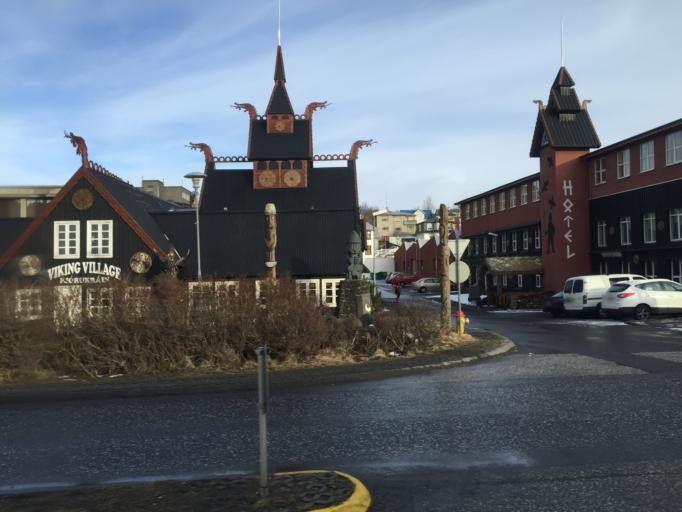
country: IS
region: Capital Region
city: Hafnarfjoerdur
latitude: 64.0653
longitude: -21.9565
